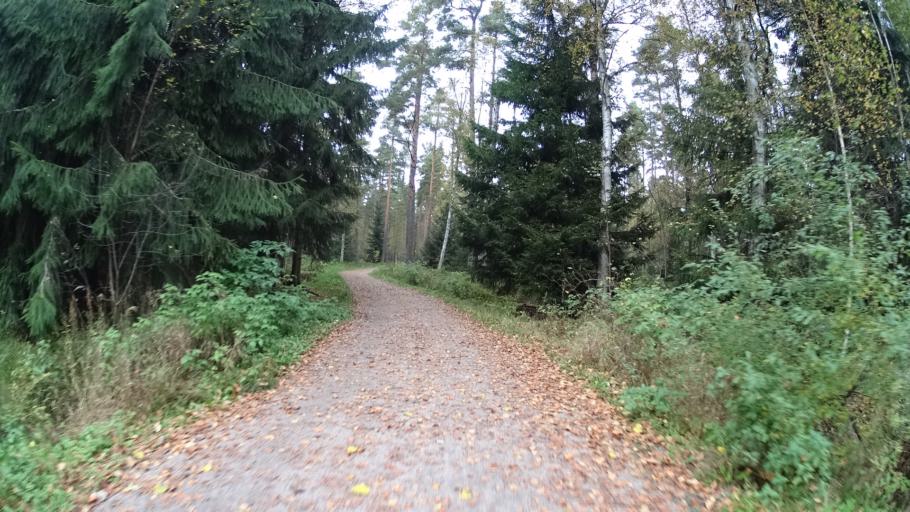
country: FI
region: Uusimaa
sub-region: Helsinki
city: Kilo
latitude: 60.1931
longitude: 24.7986
